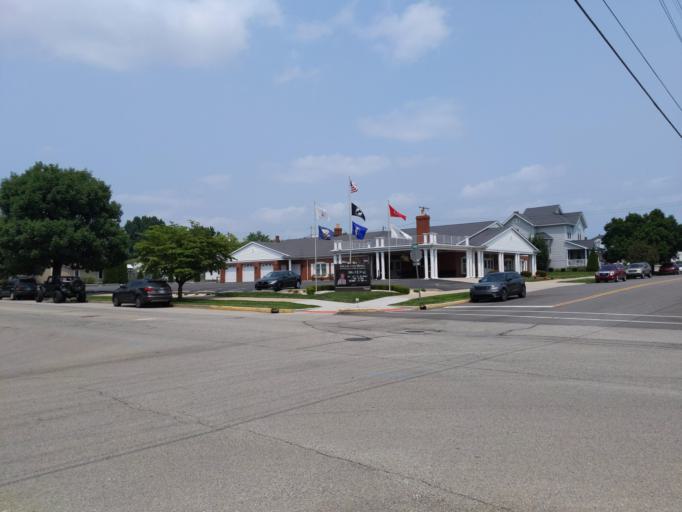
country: US
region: Indiana
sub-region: Decatur County
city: Greensburg
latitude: 39.3387
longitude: -85.4844
